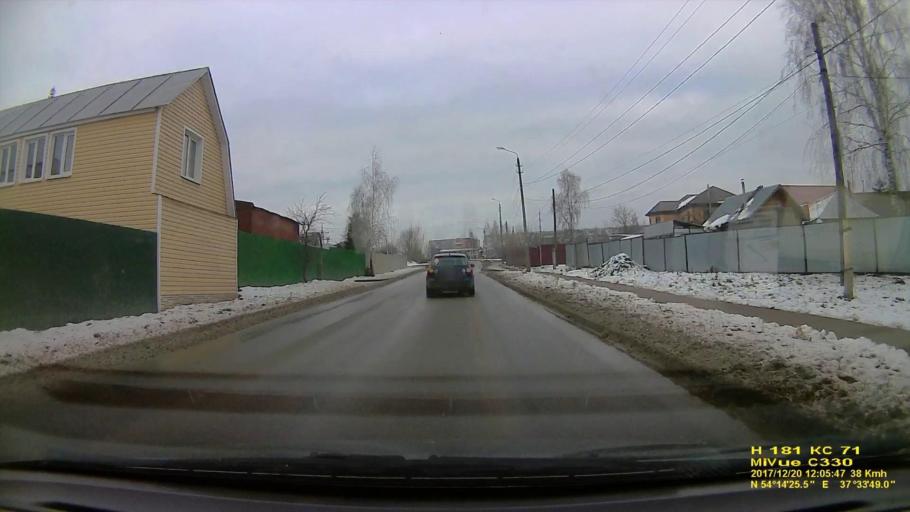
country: RU
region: Tula
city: Gorelki
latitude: 54.2404
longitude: 37.5636
